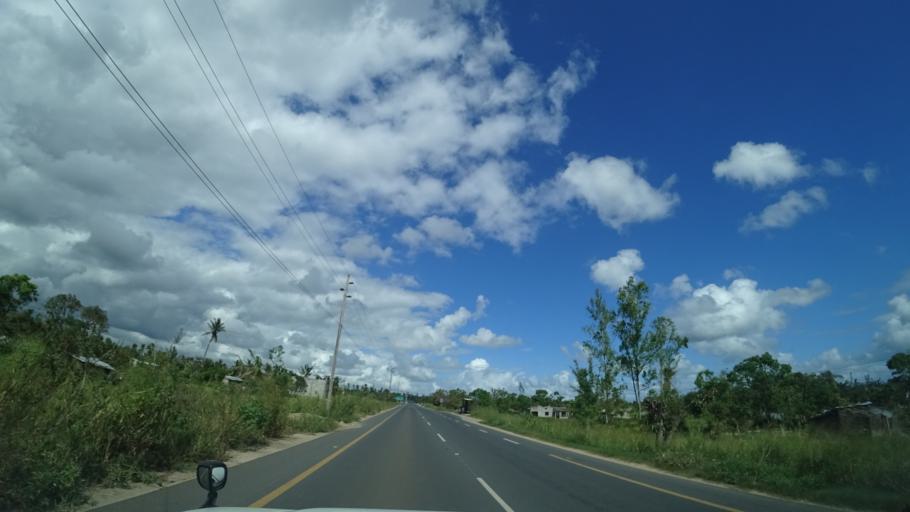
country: MZ
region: Sofala
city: Dondo
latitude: -19.5268
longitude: 34.6259
